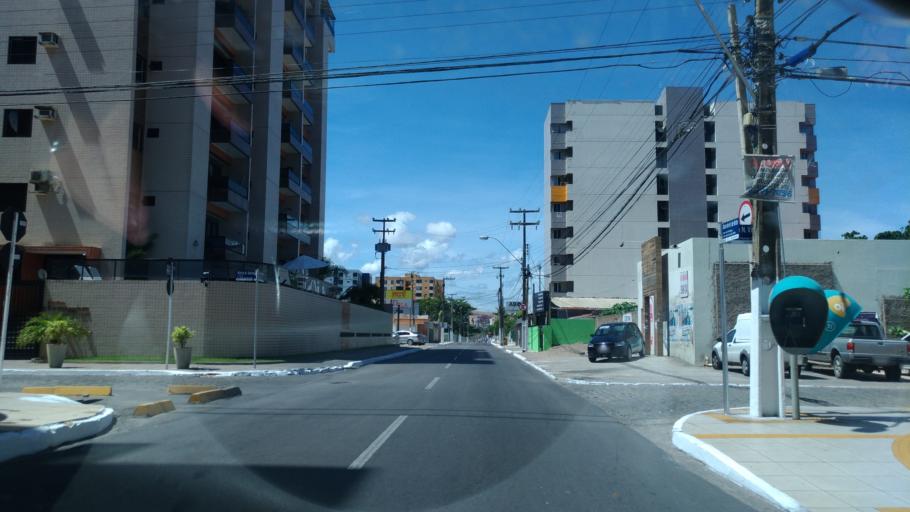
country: BR
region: Alagoas
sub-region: Maceio
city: Maceio
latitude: -9.6427
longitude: -35.7005
